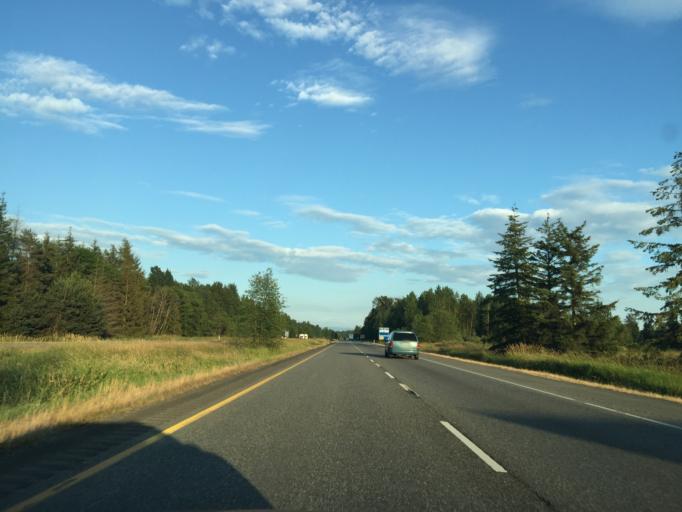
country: US
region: Washington
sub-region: Whatcom County
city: Birch Bay
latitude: 48.9471
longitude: -122.6808
